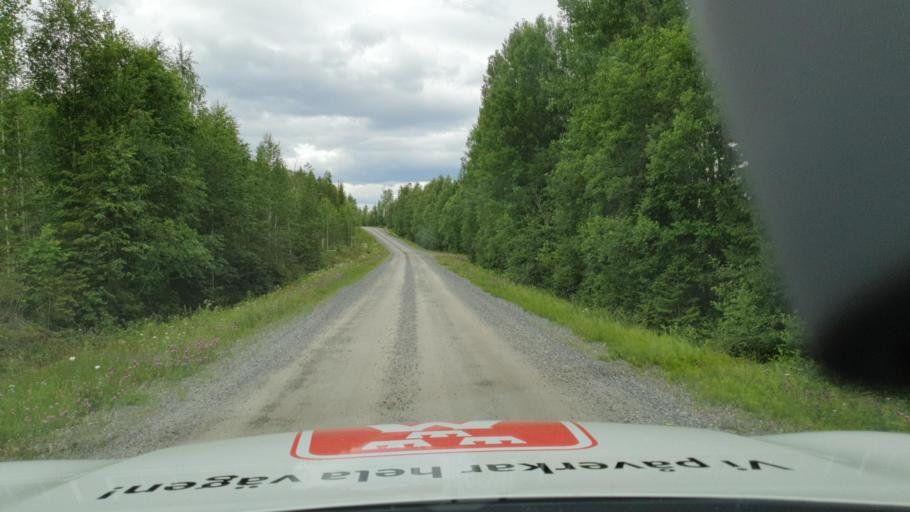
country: SE
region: Vaesterbotten
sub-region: Nordmalings Kommun
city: Nordmaling
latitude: 63.7569
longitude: 19.3688
